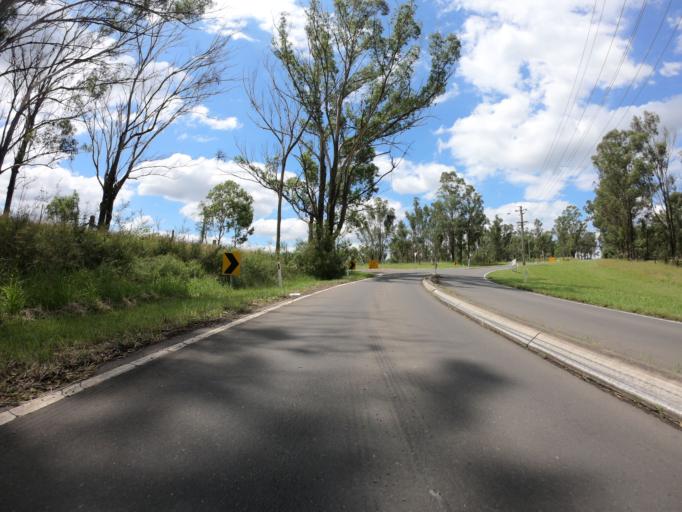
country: AU
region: New South Wales
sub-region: Penrith Municipality
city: Mulgoa
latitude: -33.8275
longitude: 150.6649
